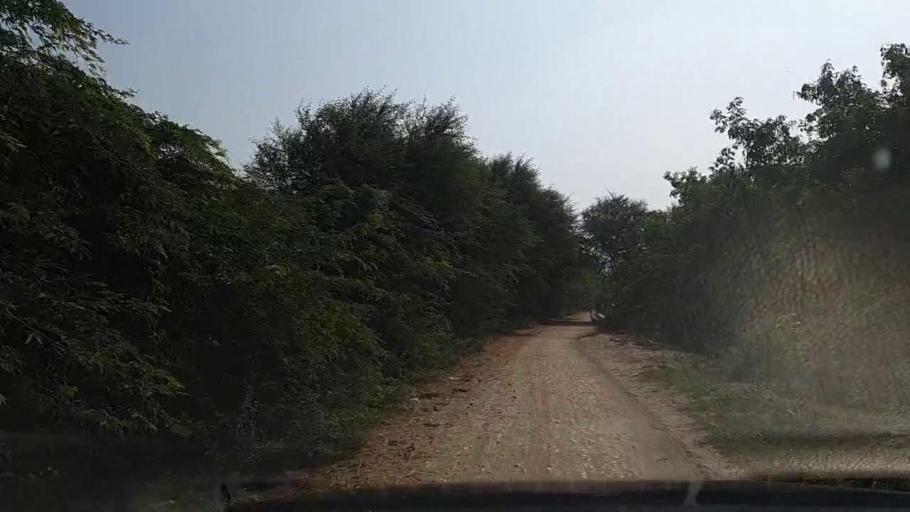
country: PK
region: Sindh
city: Mirpur Batoro
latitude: 24.6984
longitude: 68.2190
